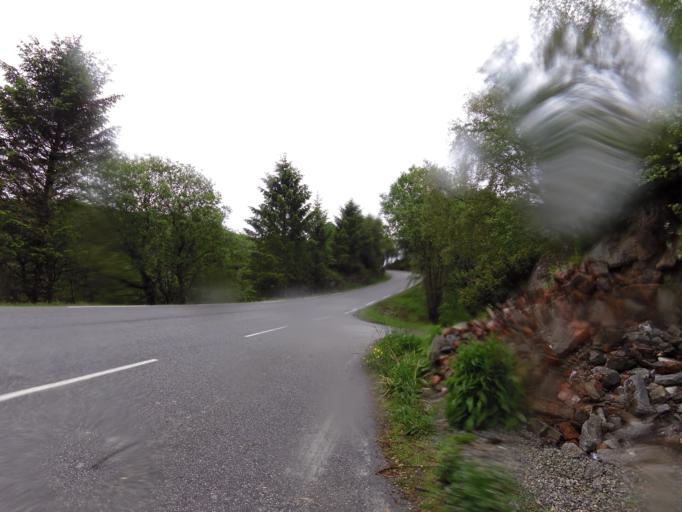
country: NO
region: Hordaland
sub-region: Sveio
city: Sveio
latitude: 59.5187
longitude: 5.2844
